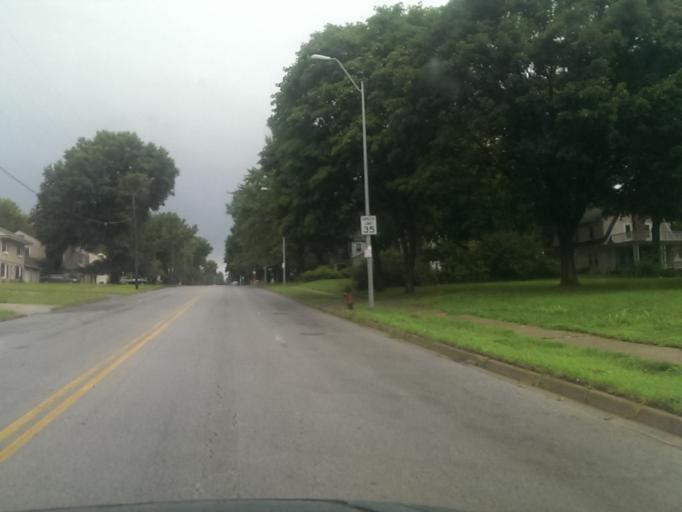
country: US
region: Kansas
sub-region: Johnson County
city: Leawood
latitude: 38.9813
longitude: -94.5807
